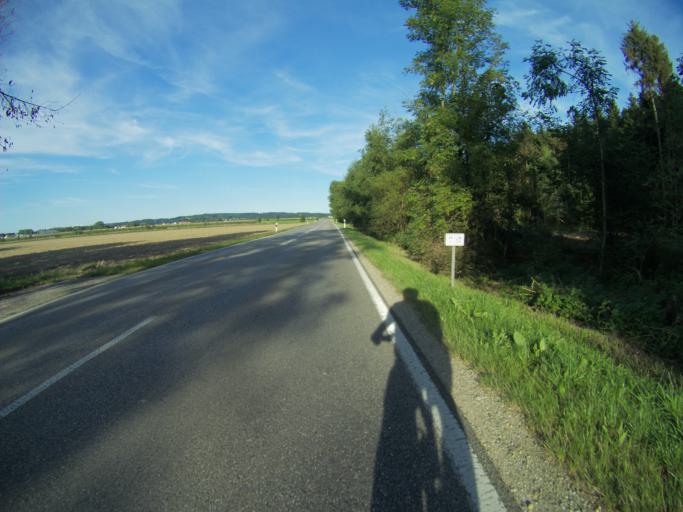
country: DE
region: Bavaria
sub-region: Upper Bavaria
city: Berglern
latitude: 48.3890
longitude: 11.9522
